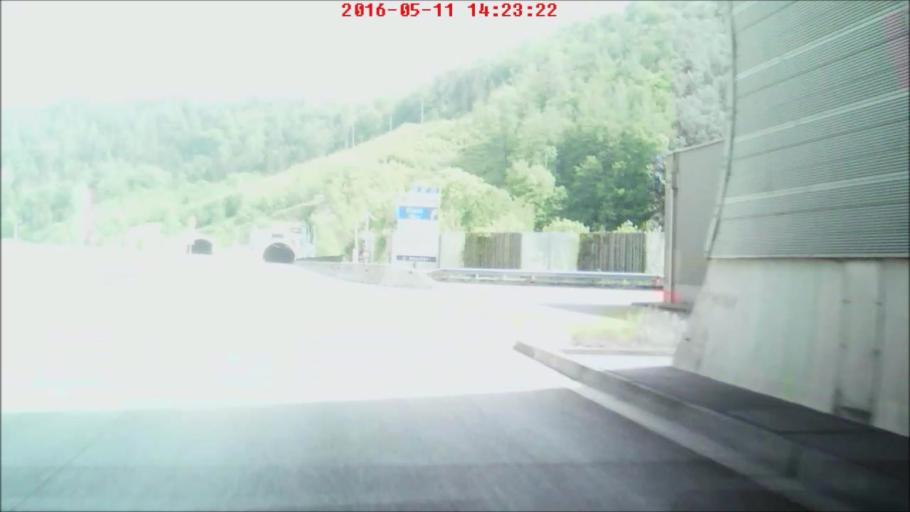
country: AT
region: Upper Austria
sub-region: Politischer Bezirk Kirchdorf an der Krems
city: Micheldorf in Oberoesterreich
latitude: 47.8518
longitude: 14.1610
